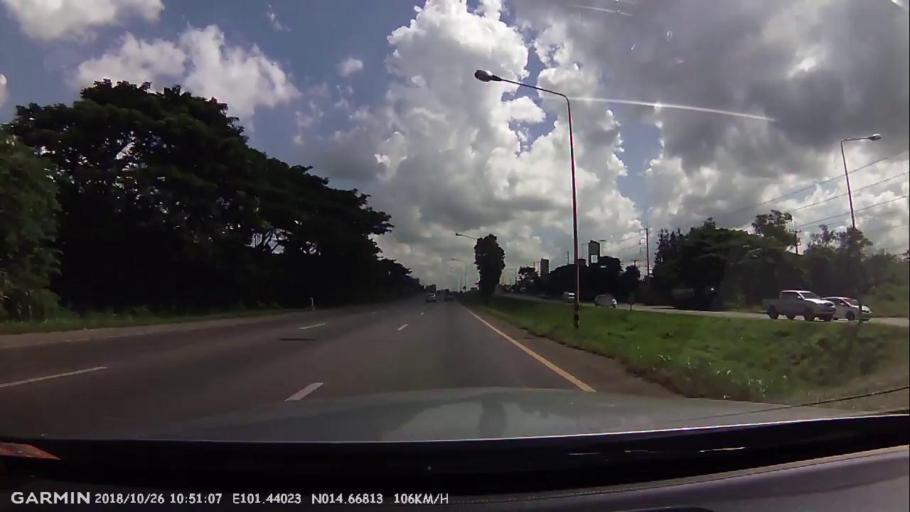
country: TH
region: Nakhon Ratchasima
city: Pak Chong
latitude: 14.6683
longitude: 101.4405
